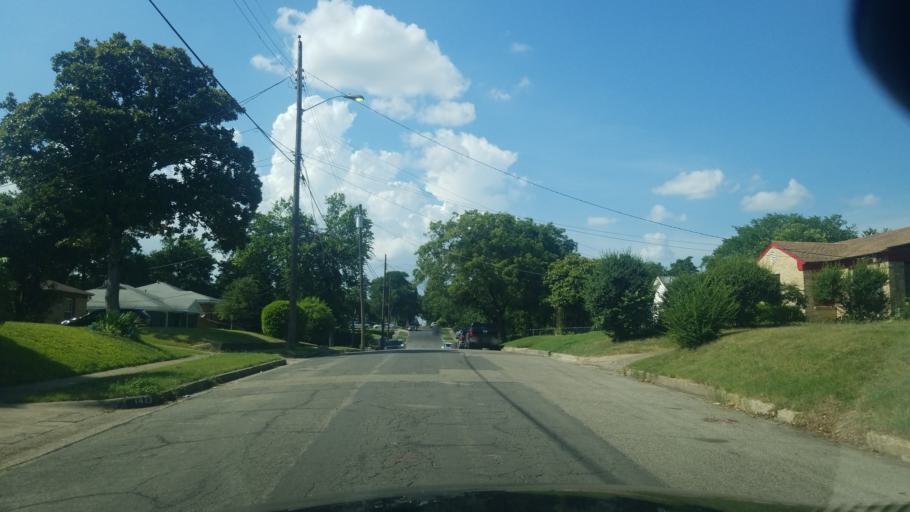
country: US
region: Texas
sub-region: Dallas County
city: Dallas
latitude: 32.7304
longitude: -96.8091
